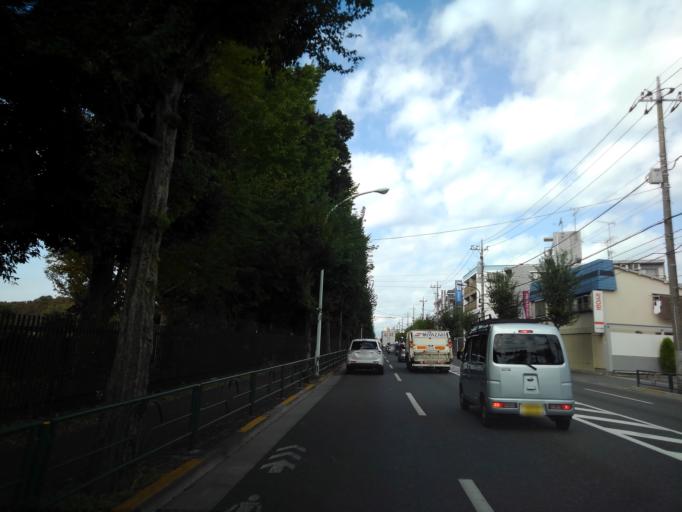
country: JP
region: Tokyo
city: Higashimurayama-shi
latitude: 35.7468
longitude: 139.4844
